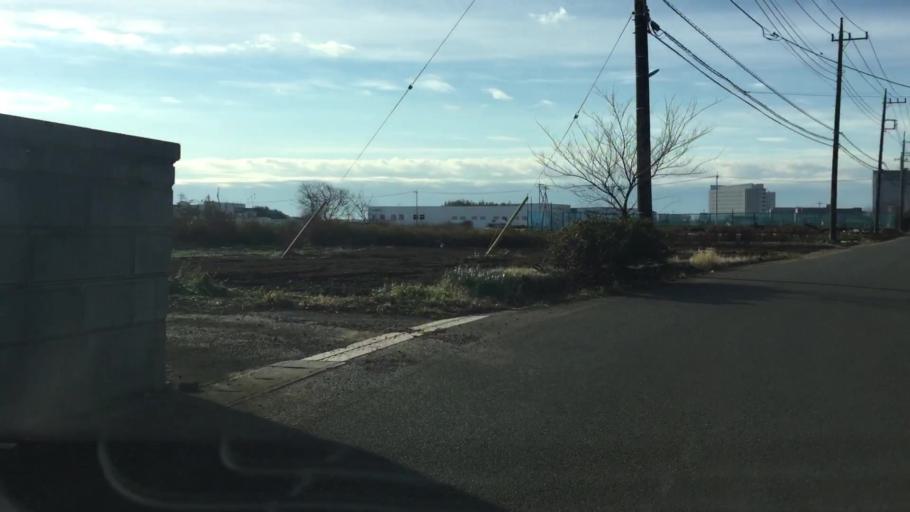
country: JP
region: Chiba
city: Shiroi
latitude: 35.8193
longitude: 140.1272
